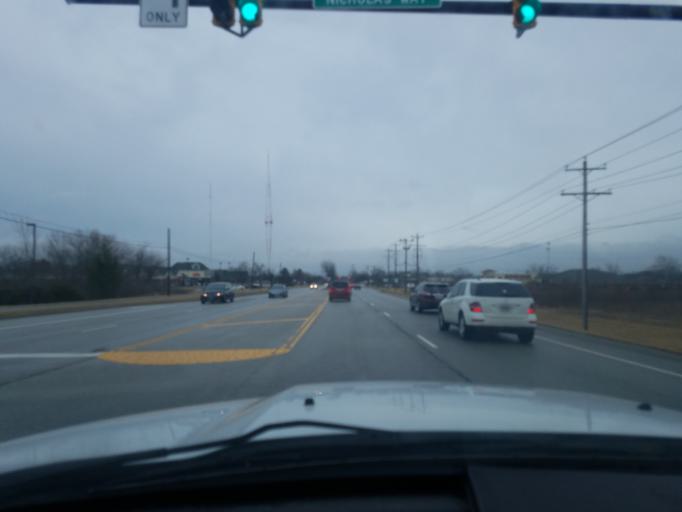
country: US
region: Ohio
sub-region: Warren County
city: Mason
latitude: 39.3520
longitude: -84.3352
